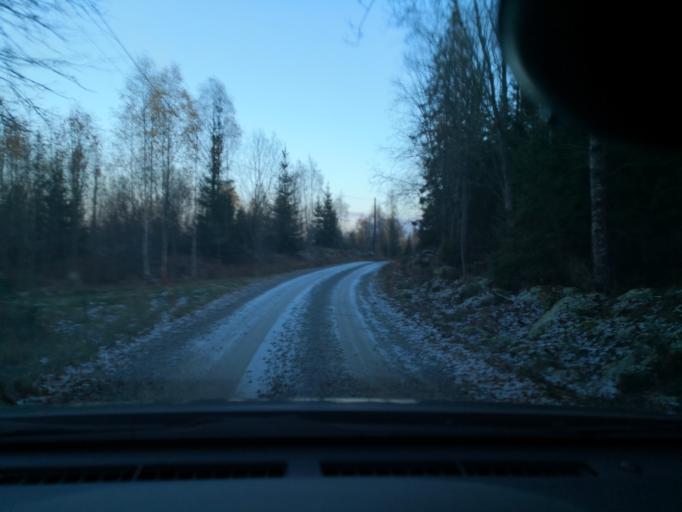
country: SE
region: Vaestmanland
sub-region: Vasteras
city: Tillberga
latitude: 59.7638
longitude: 16.6288
